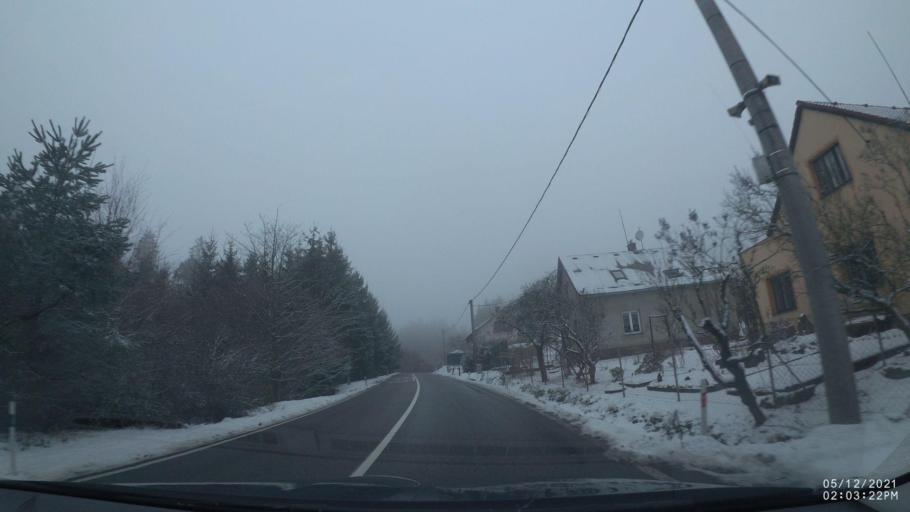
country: CZ
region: Kralovehradecky
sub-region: Okres Nachod
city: Cerveny Kostelec
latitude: 50.4892
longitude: 16.1318
